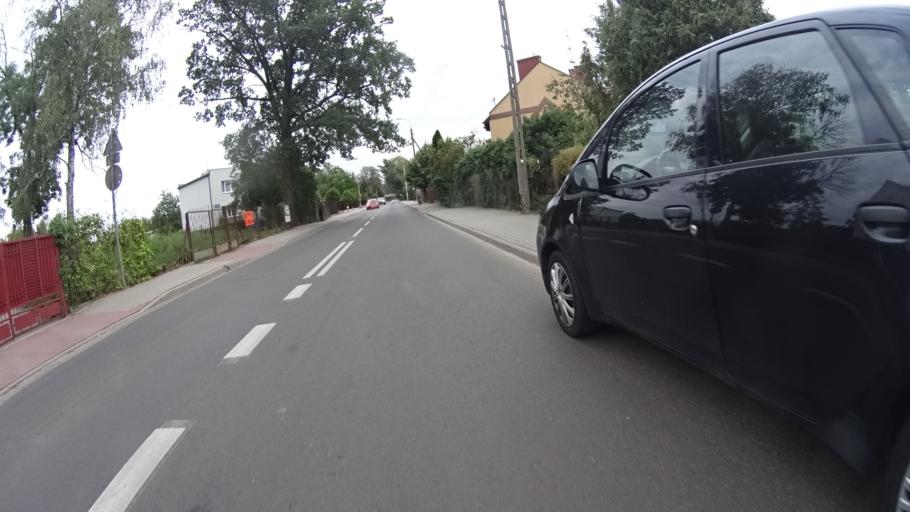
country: PL
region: Masovian Voivodeship
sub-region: Powiat pruszkowski
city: Granica
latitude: 52.1428
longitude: 20.7924
